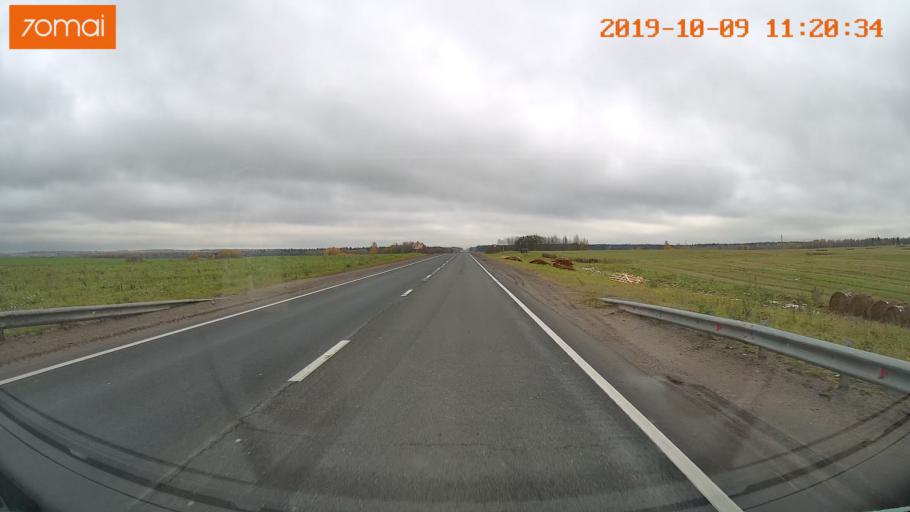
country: RU
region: Vologda
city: Vologda
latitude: 59.1483
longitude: 39.9399
